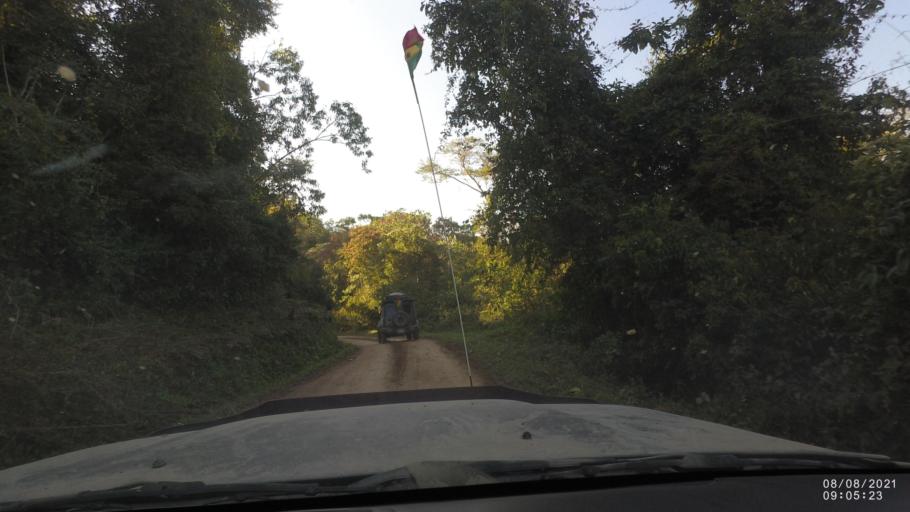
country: BO
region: La Paz
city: Quime
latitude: -16.5575
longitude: -66.7378
